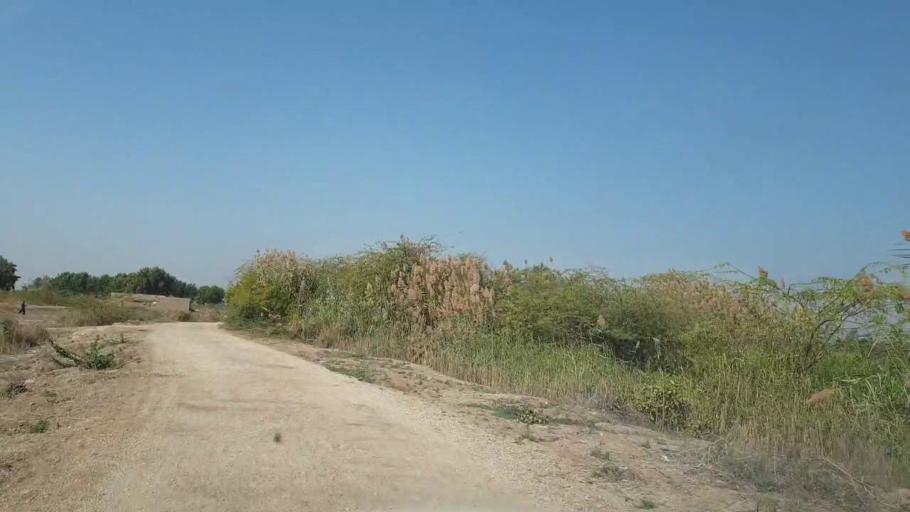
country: PK
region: Sindh
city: Mirpur Khas
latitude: 25.5286
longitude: 69.0482
